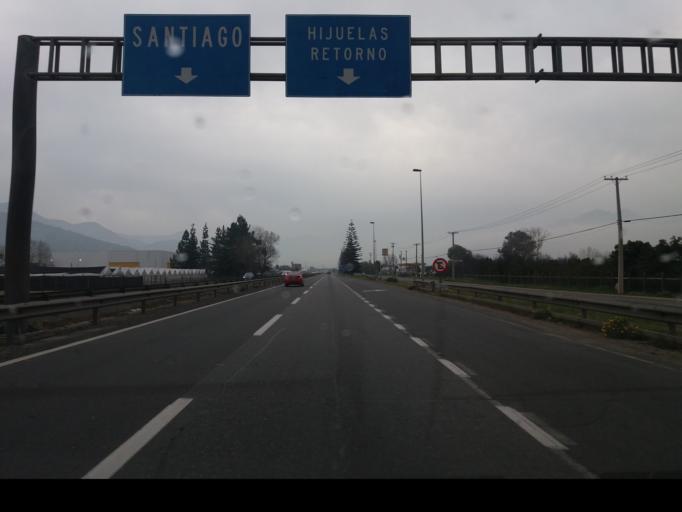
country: CL
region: Valparaiso
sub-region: Provincia de Quillota
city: Hacienda La Calera
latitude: -32.7963
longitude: -71.1599
